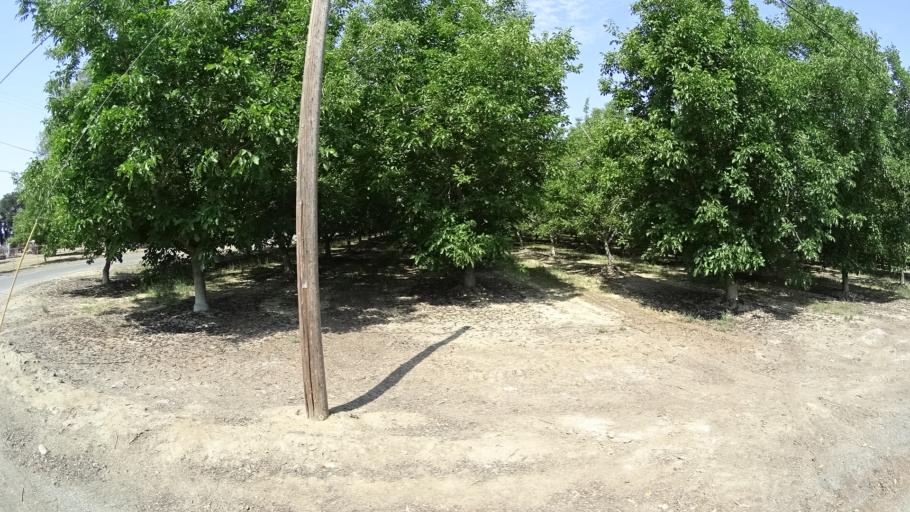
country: US
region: California
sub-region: Fresno County
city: Laton
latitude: 36.3950
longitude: -119.7624
